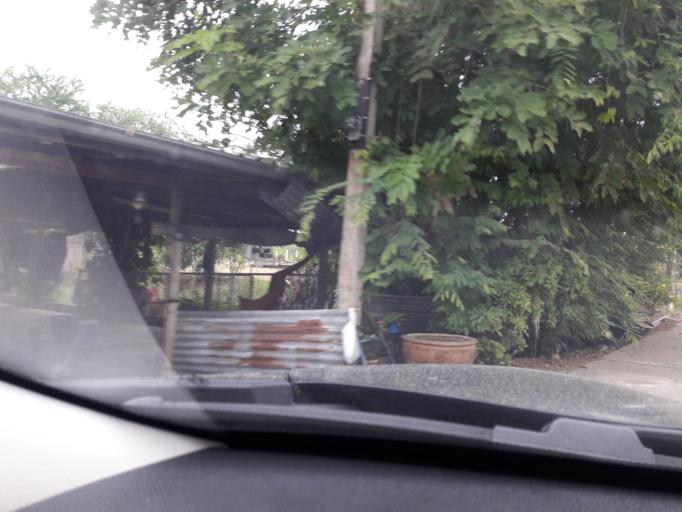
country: TH
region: Ratchaburi
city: Bang Phae
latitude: 13.6310
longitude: 99.9412
